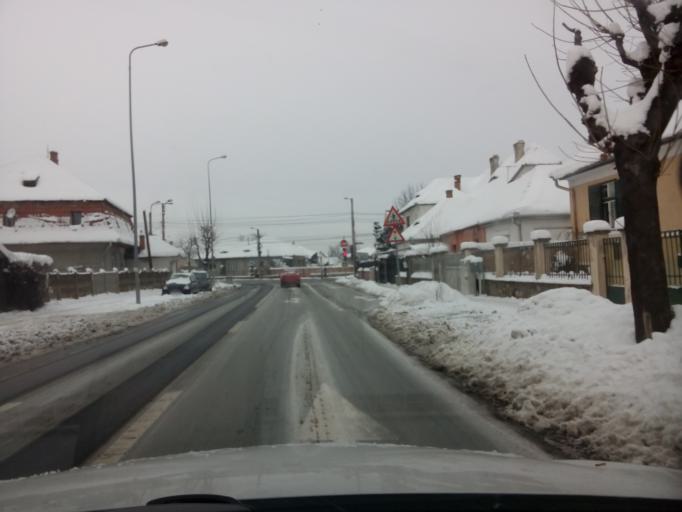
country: RO
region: Sibiu
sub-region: Municipiul Sibiu
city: Sibiu
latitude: 45.7894
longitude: 24.1640
